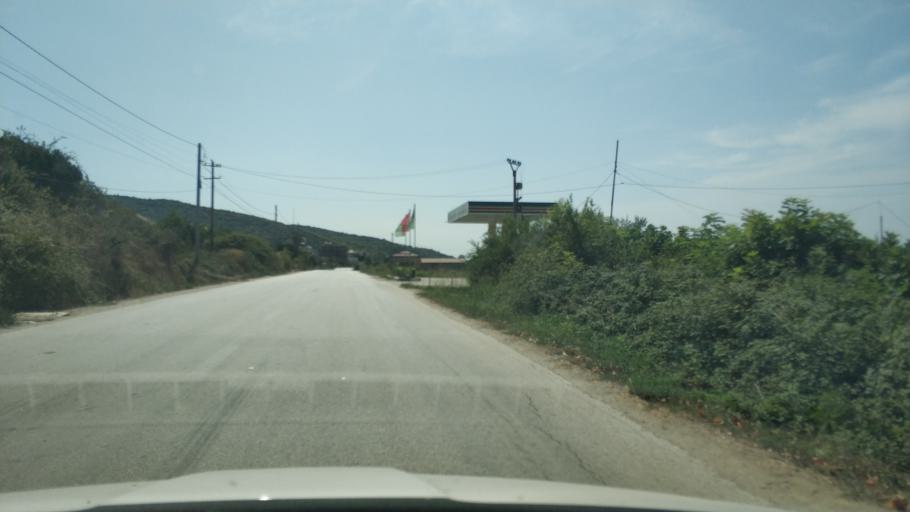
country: AL
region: Fier
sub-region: Rrethi i Lushnjes
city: Grabjan
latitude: 40.9443
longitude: 19.5373
